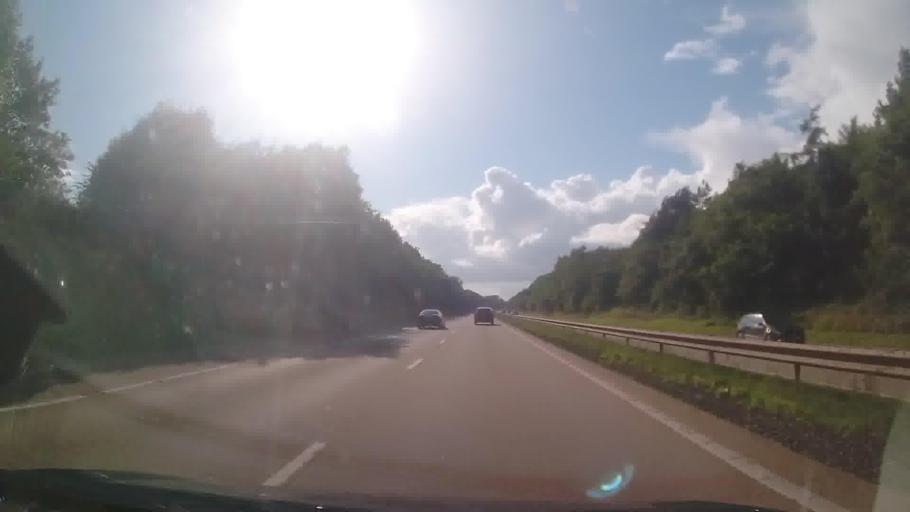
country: GB
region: England
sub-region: Shropshire
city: Albrighton
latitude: 52.6499
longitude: -2.2519
